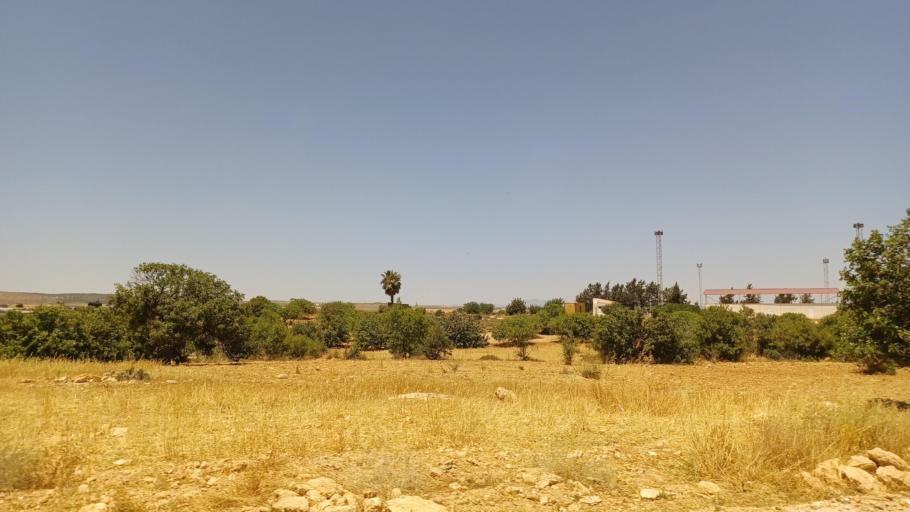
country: CY
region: Larnaka
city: Pyla
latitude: 35.0240
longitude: 33.7027
